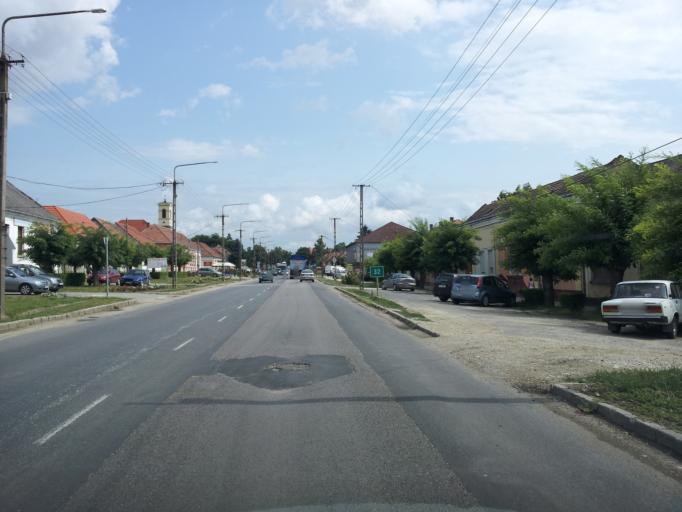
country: HU
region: Fejer
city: Enying
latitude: 46.9306
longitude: 18.2420
